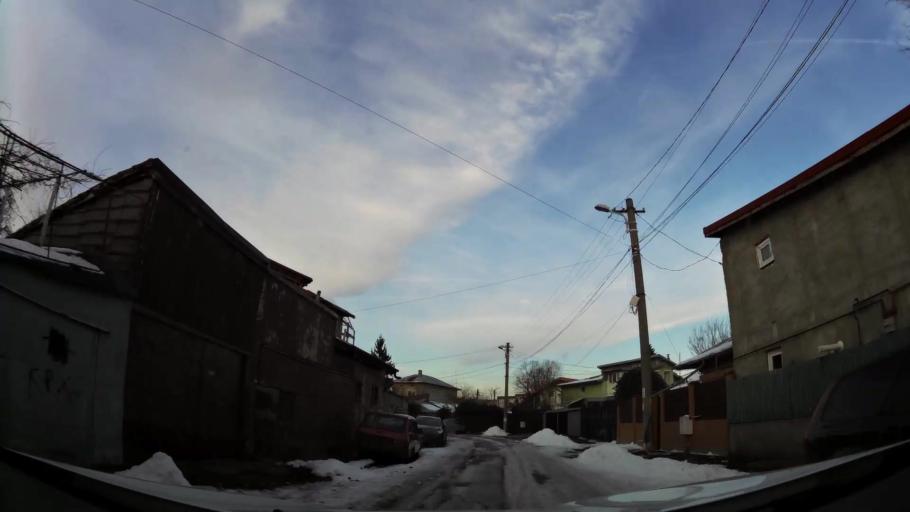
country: RO
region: Bucuresti
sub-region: Municipiul Bucuresti
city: Bucuresti
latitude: 44.3946
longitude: 26.0812
